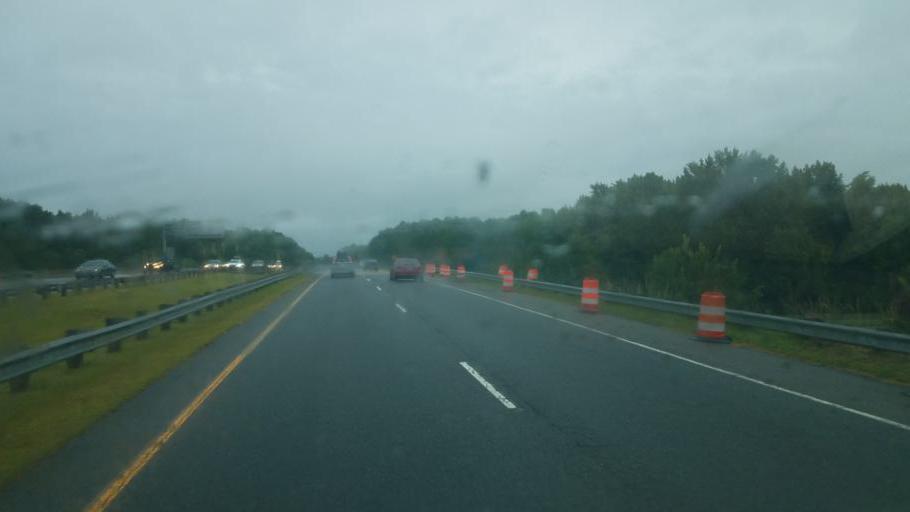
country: US
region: Virginia
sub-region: City of Chesapeake
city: Chesapeake
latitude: 36.7068
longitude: -76.2261
